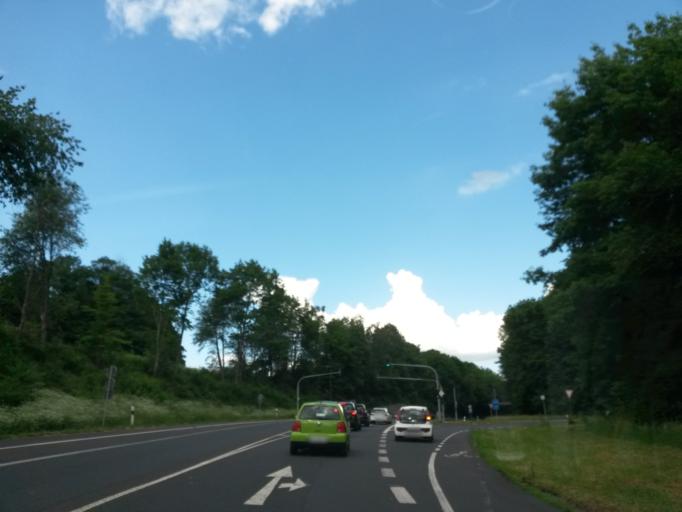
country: DE
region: North Rhine-Westphalia
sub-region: Regierungsbezirk Koln
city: Hennef
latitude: 50.8477
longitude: 7.2943
